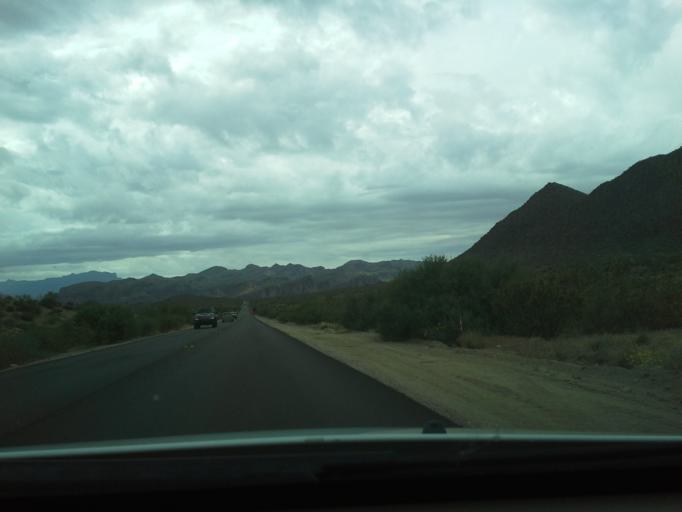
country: US
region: Arizona
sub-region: Maricopa County
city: Fountain Hills
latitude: 33.6036
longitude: -111.5471
